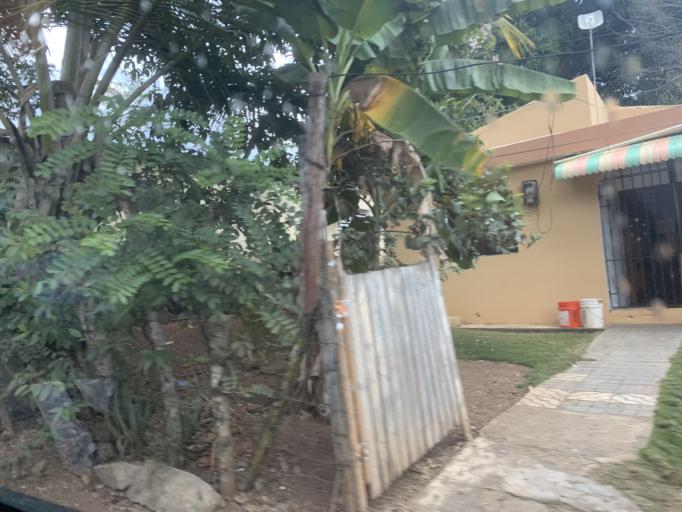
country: DO
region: Monte Plata
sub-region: Yamasa
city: Yamasa
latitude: 18.7719
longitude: -70.0217
